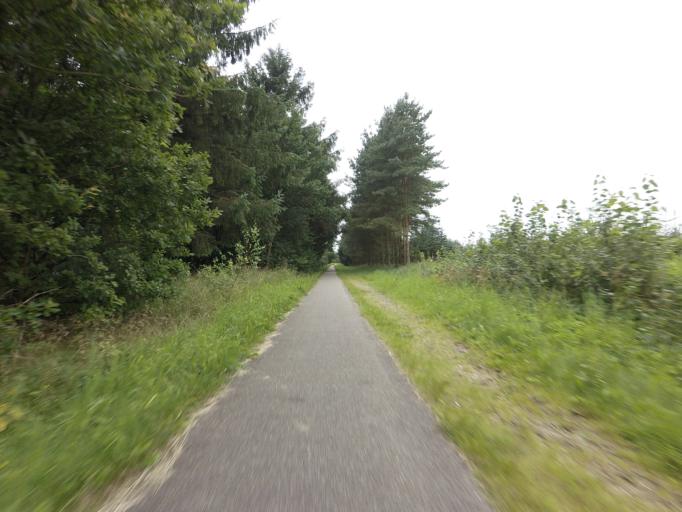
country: DK
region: Central Jutland
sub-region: Silkeborg Kommune
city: Virklund
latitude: 56.0687
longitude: 9.5019
